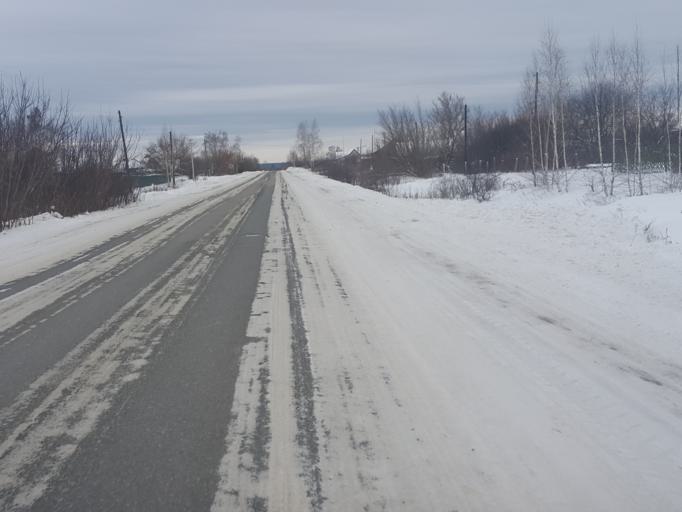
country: RU
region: Tambov
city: Platonovka
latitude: 52.8640
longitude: 41.8487
